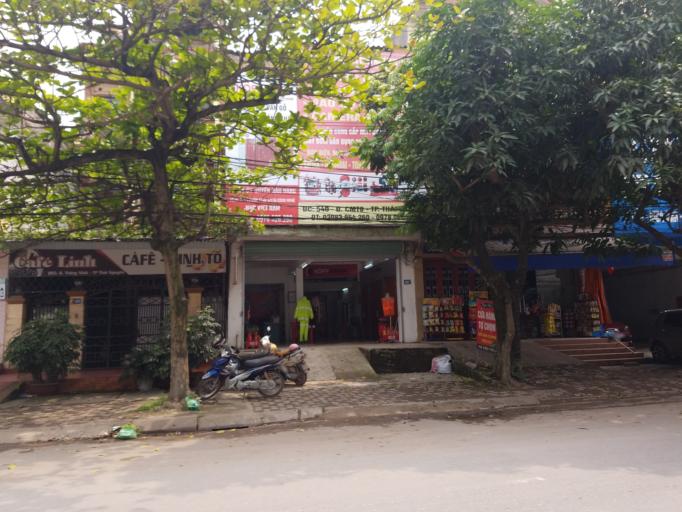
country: VN
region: Thai Nguyen
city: Thanh Pho Thai Nguyen
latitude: 21.5786
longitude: 105.8371
